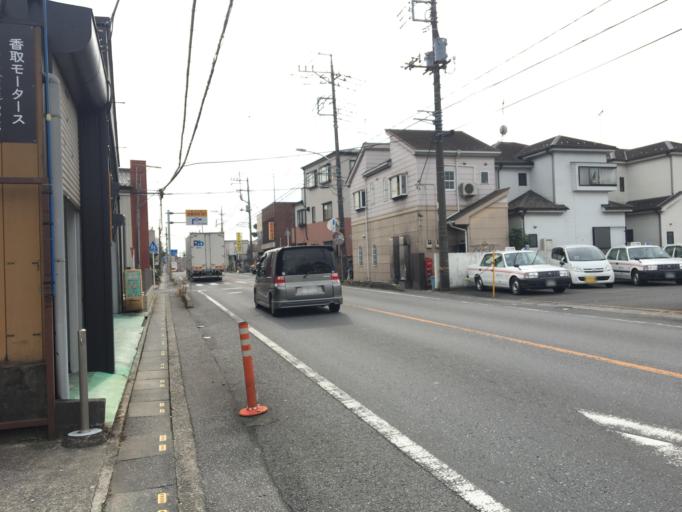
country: JP
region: Saitama
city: Yoshikawa
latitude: 35.8879
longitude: 139.8408
